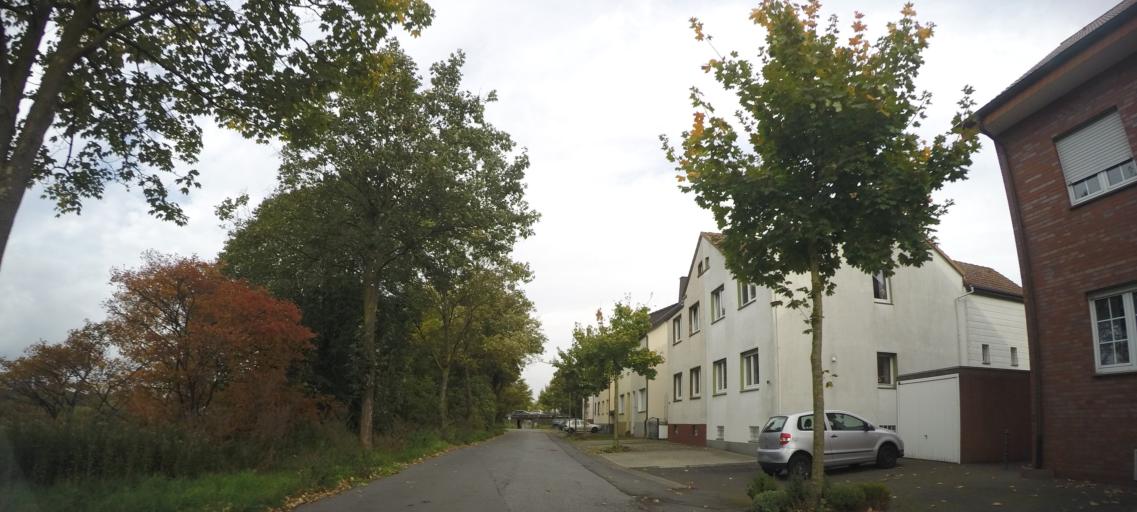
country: DE
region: North Rhine-Westphalia
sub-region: Regierungsbezirk Arnsberg
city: Lippstadt
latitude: 51.6773
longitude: 8.3649
